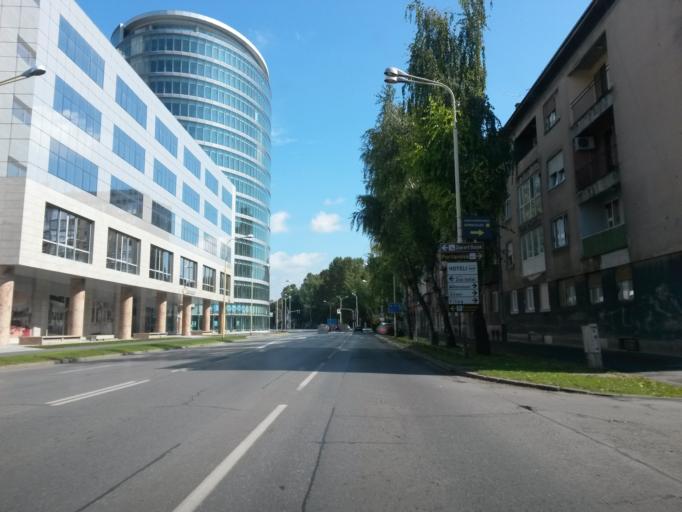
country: HR
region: Osjecko-Baranjska
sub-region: Grad Osijek
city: Osijek
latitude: 45.5553
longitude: 18.6932
